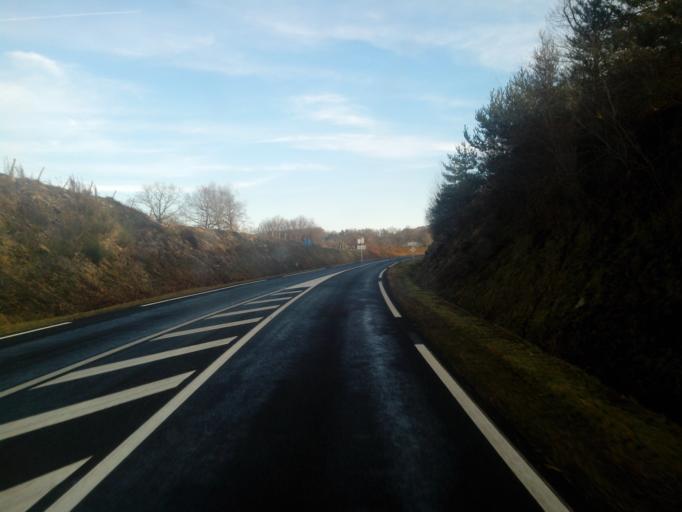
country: FR
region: Limousin
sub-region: Departement de la Correze
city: Bort-les-Orgues
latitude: 45.3571
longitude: 2.5090
